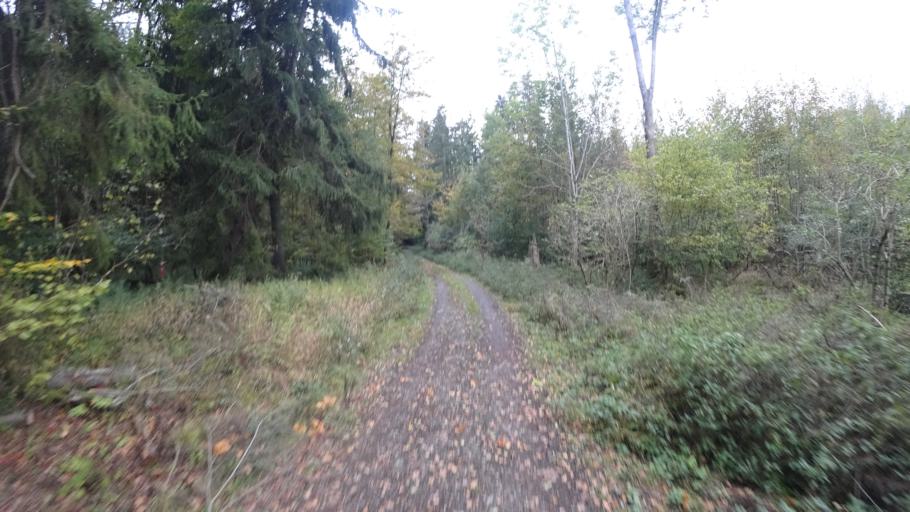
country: DE
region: Rheinland-Pfalz
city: Ruckeroth
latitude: 50.5516
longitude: 7.7576
